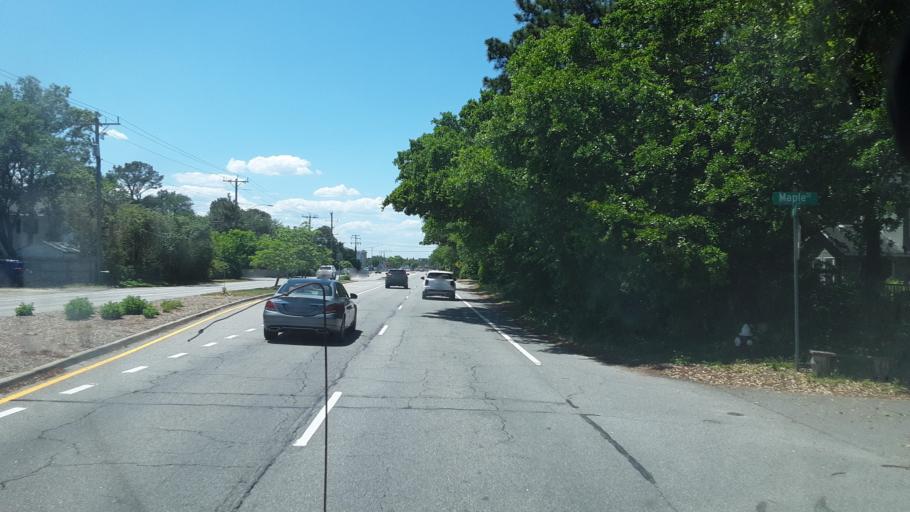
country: US
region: Virginia
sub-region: City of Virginia Beach
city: Virginia Beach
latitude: 36.9135
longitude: -76.0639
